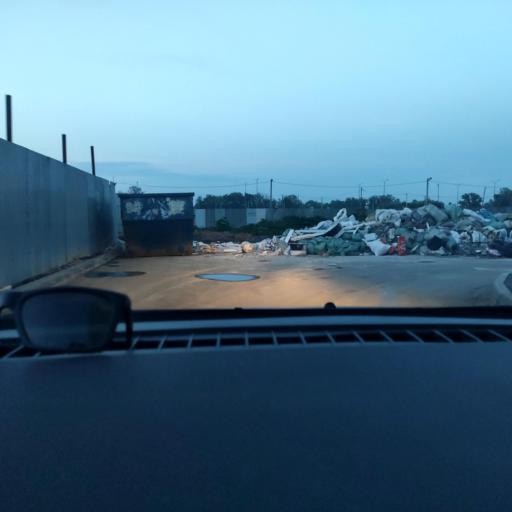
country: RU
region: Samara
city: Samara
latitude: 53.1439
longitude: 50.0745
